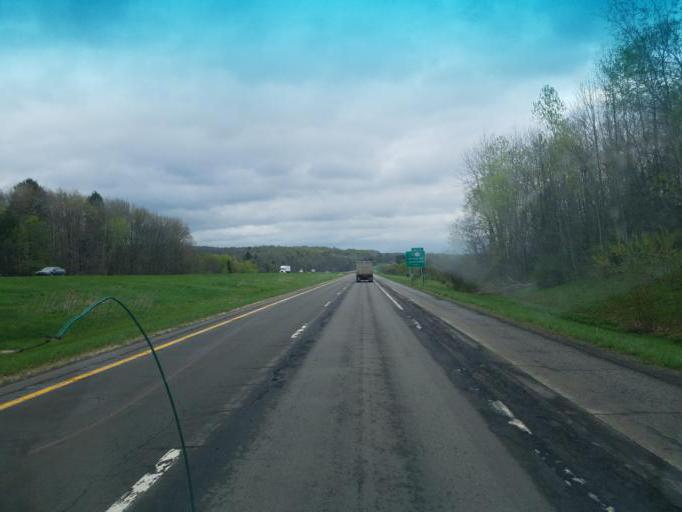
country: US
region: New York
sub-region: Chautauqua County
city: Celoron
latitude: 42.1280
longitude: -79.3007
